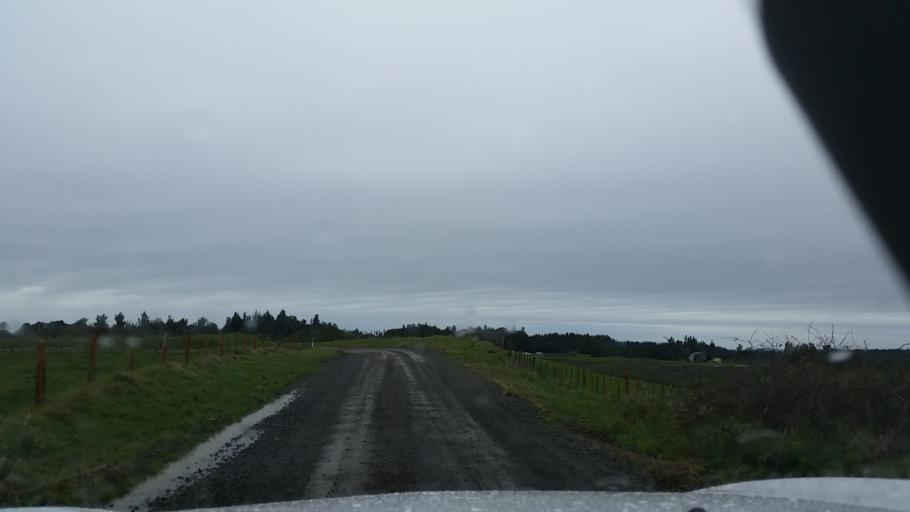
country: NZ
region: Bay of Plenty
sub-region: Western Bay of Plenty District
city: Maketu
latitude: -37.9715
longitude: 176.4361
